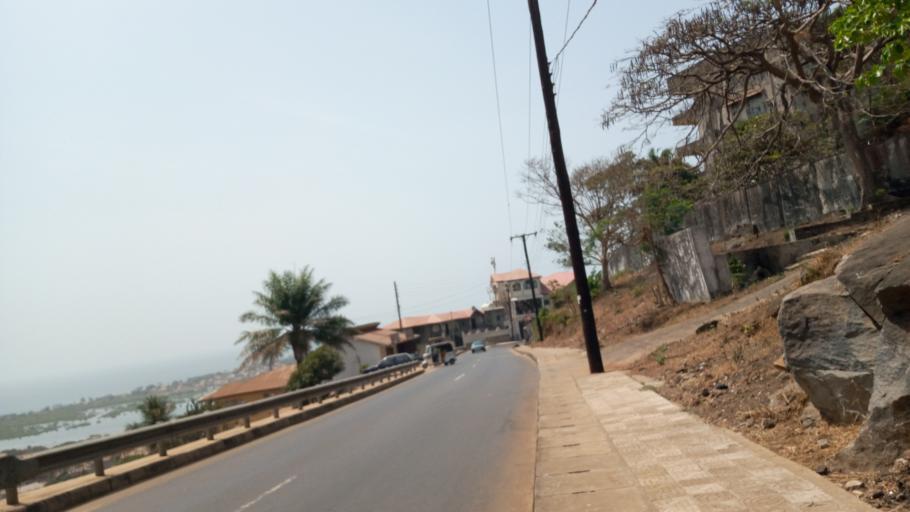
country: SL
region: Western Area
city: Freetown
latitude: 8.4822
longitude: -13.2663
